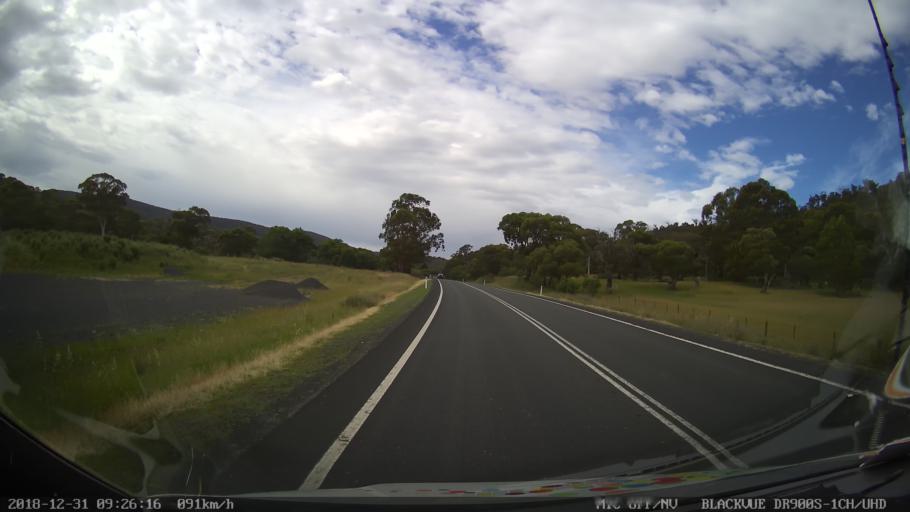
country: AU
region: New South Wales
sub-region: Snowy River
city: Jindabyne
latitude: -36.4451
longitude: 148.4959
